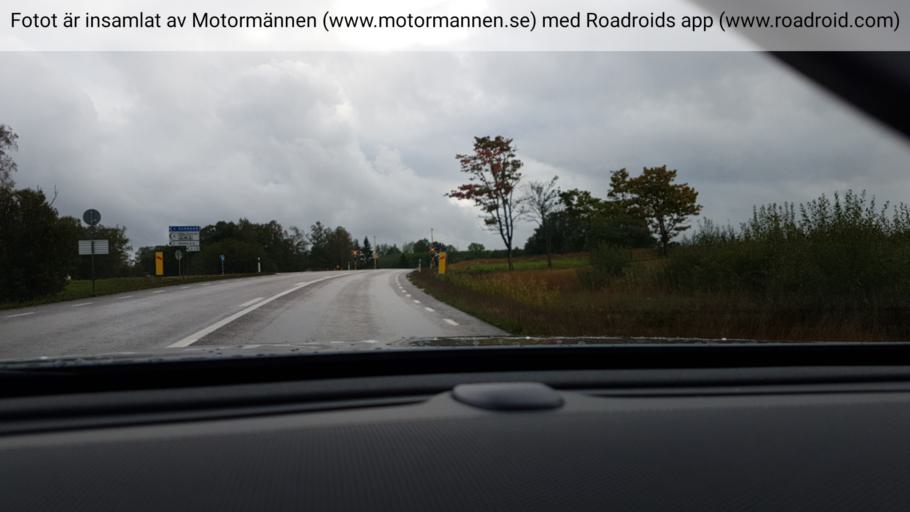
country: SE
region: Vaestra Goetaland
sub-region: Melleruds Kommun
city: Mellerud
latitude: 58.7210
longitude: 12.4561
